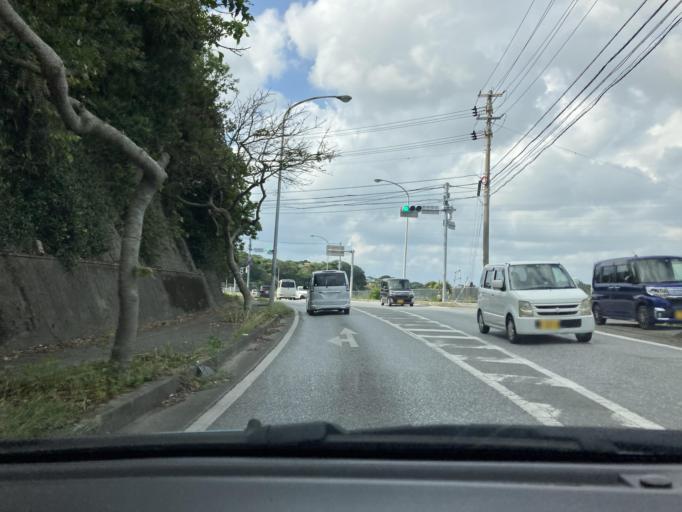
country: JP
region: Okinawa
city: Chatan
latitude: 26.2888
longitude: 127.7862
